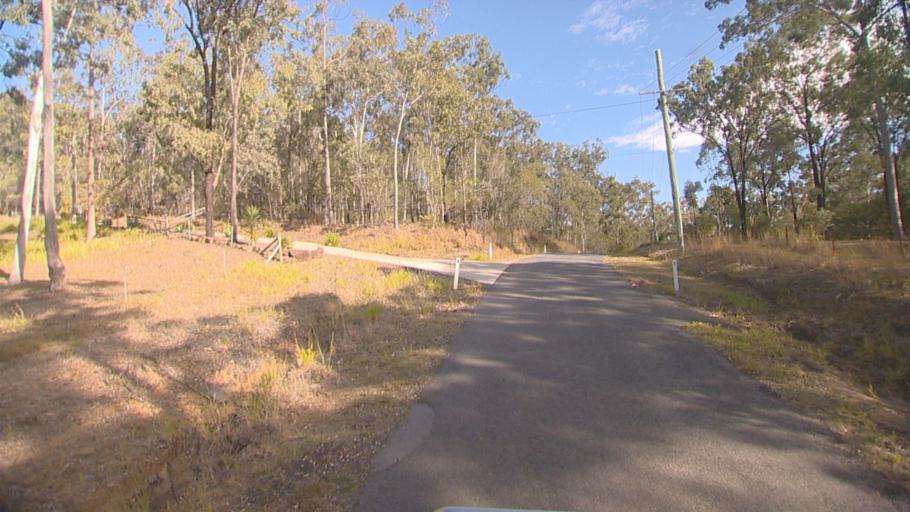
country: AU
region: Queensland
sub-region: Logan
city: Chambers Flat
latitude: -27.8245
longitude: 153.0796
